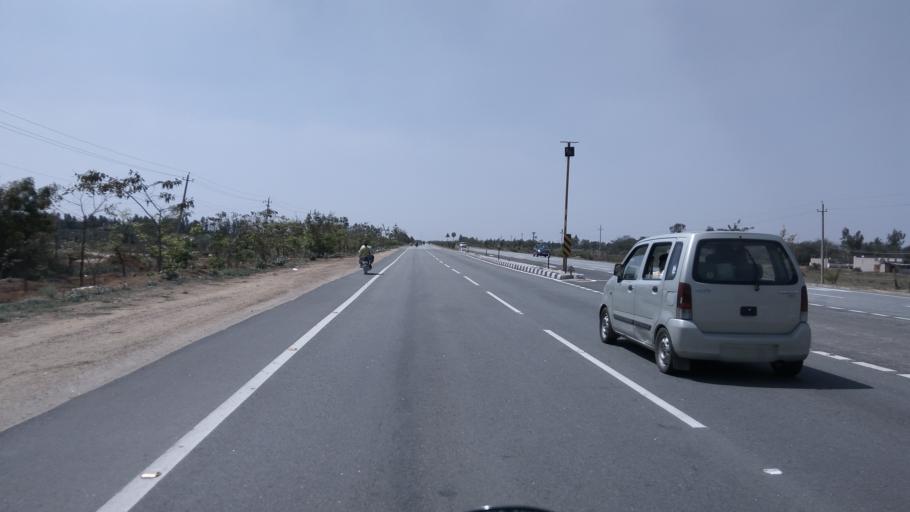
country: IN
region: Karnataka
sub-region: Kolar
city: Mulbagal
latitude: 13.1510
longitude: 78.3846
